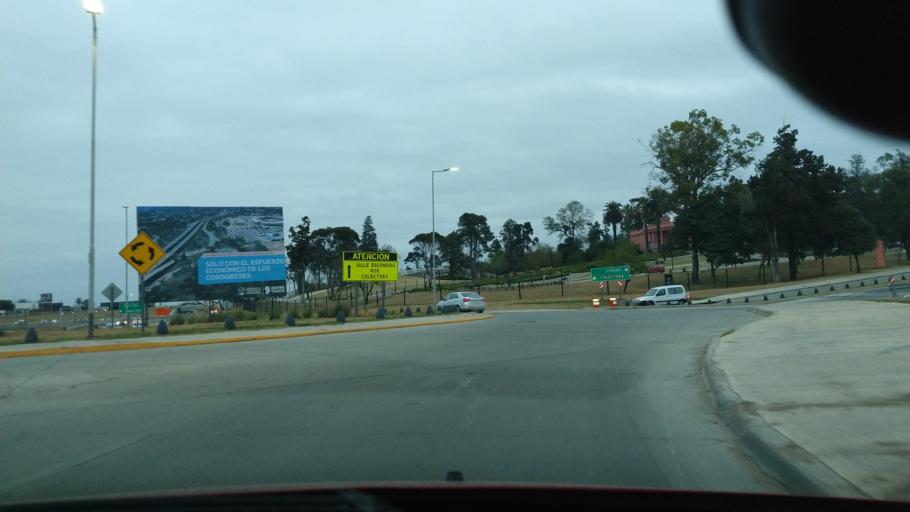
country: AR
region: Cordoba
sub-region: Departamento de Capital
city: Cordoba
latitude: -31.3721
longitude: -64.2532
